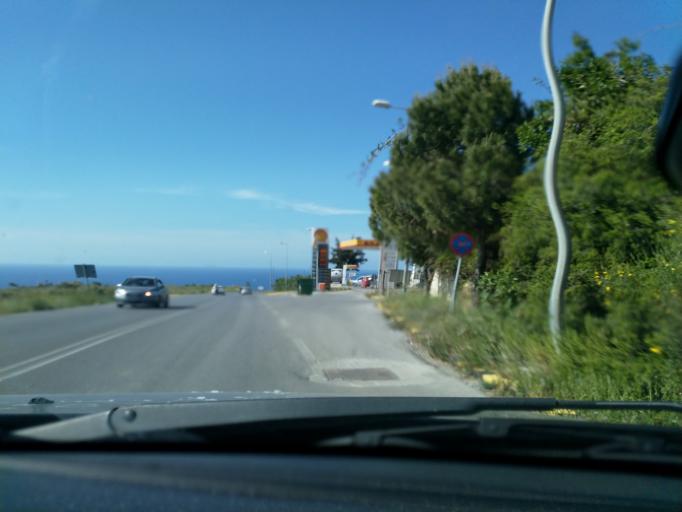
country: GR
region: Crete
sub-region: Nomos Rethymnis
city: Rethymno
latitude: 35.3527
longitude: 24.4613
